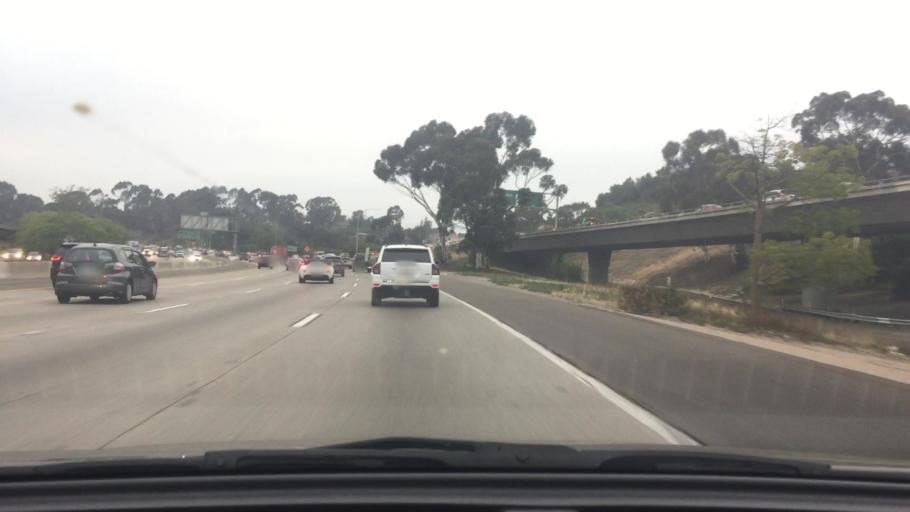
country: US
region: California
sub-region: San Diego County
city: National City
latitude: 32.7226
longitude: -117.1019
